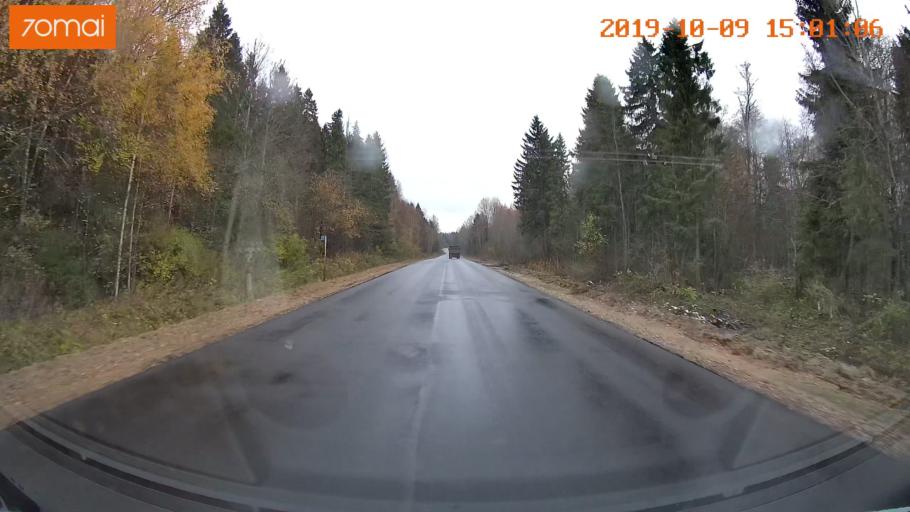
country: RU
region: Kostroma
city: Chistyye Bory
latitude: 58.3013
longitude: 41.6789
